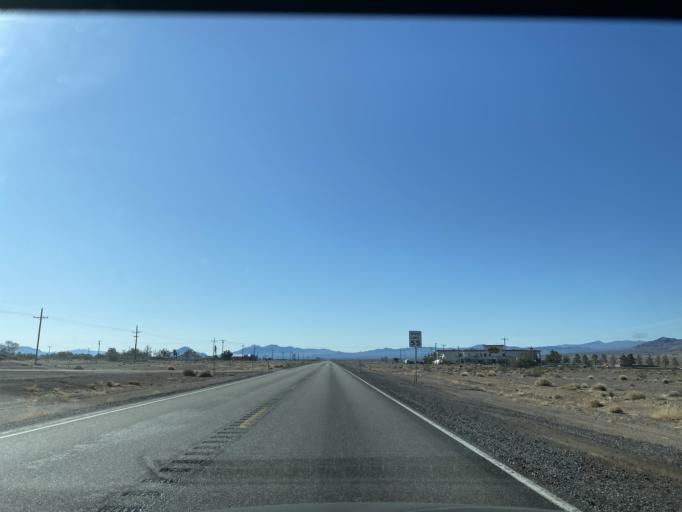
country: US
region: Nevada
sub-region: Nye County
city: Pahrump
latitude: 36.4167
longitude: -116.4222
